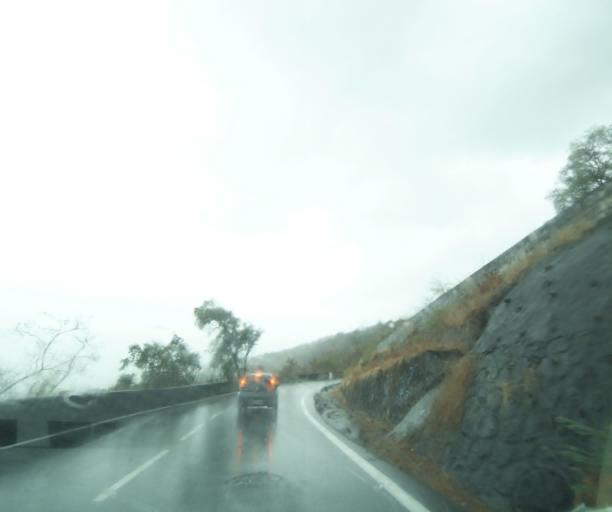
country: RE
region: Reunion
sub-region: Reunion
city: Saint-Paul
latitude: -21.0154
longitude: 55.2719
